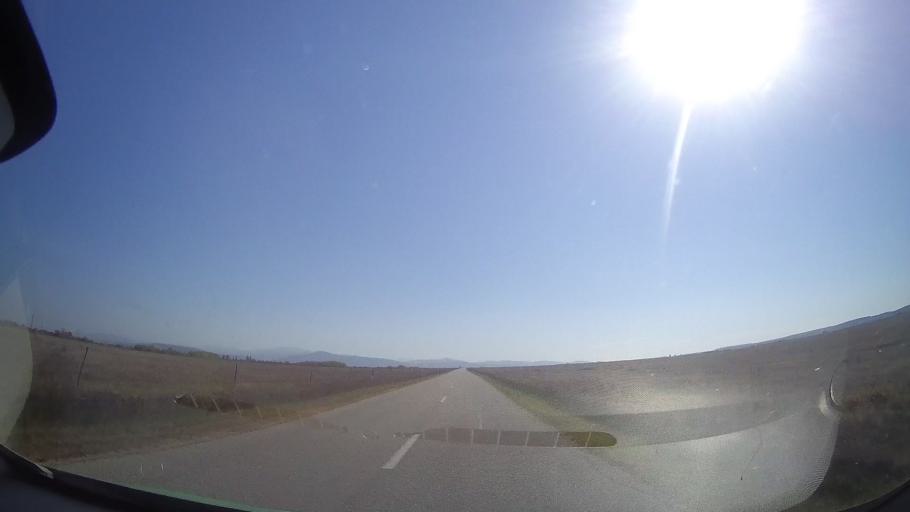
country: RO
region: Timis
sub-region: Comuna Traian Vuia
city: Traian Vuia
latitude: 45.7995
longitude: 22.0097
